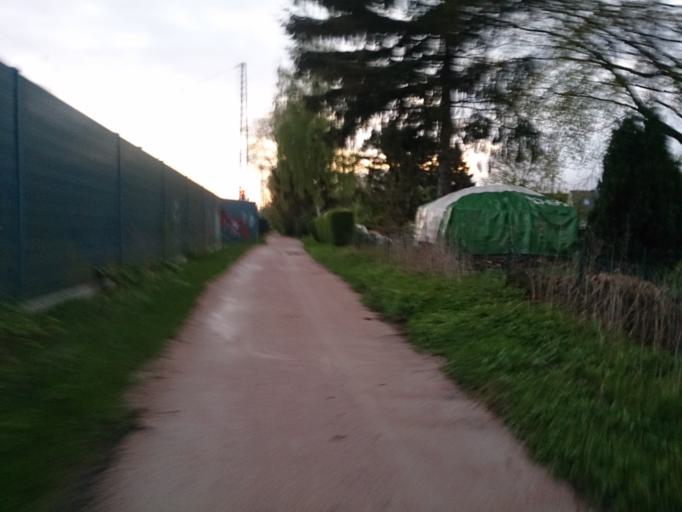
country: DE
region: Hamburg
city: Harburg
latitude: 53.4723
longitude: 9.9066
